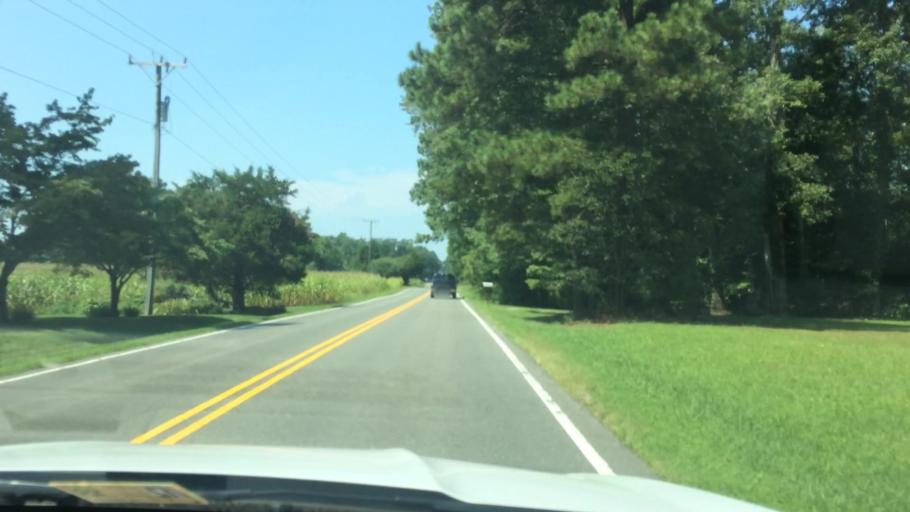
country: US
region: Virginia
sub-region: Henrico County
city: Sandston
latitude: 37.5280
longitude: -77.1637
